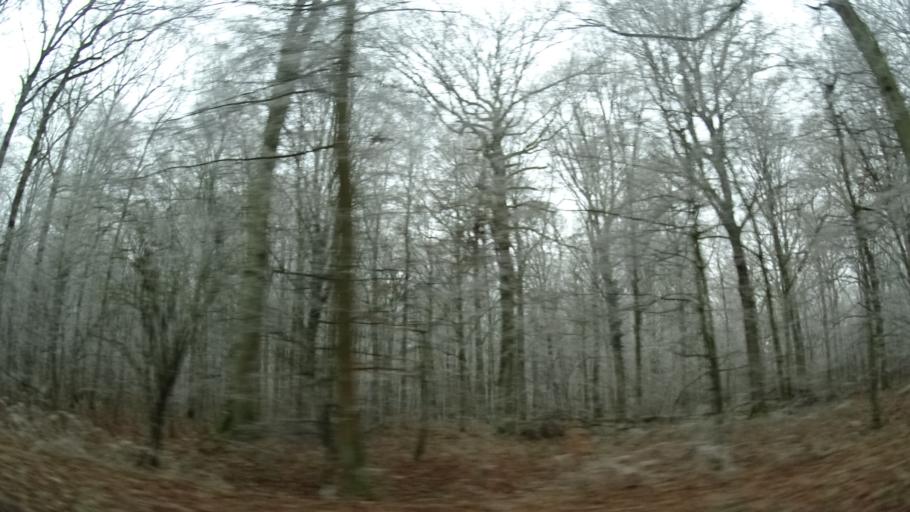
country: DE
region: Bavaria
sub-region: Regierungsbezirk Unterfranken
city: Butthard
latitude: 49.5805
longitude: 9.8655
